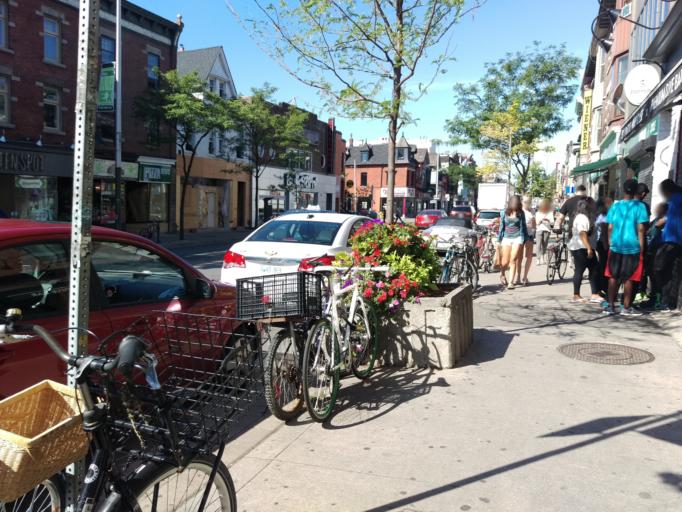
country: CA
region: Ontario
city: Toronto
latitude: 43.6659
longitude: -79.4079
